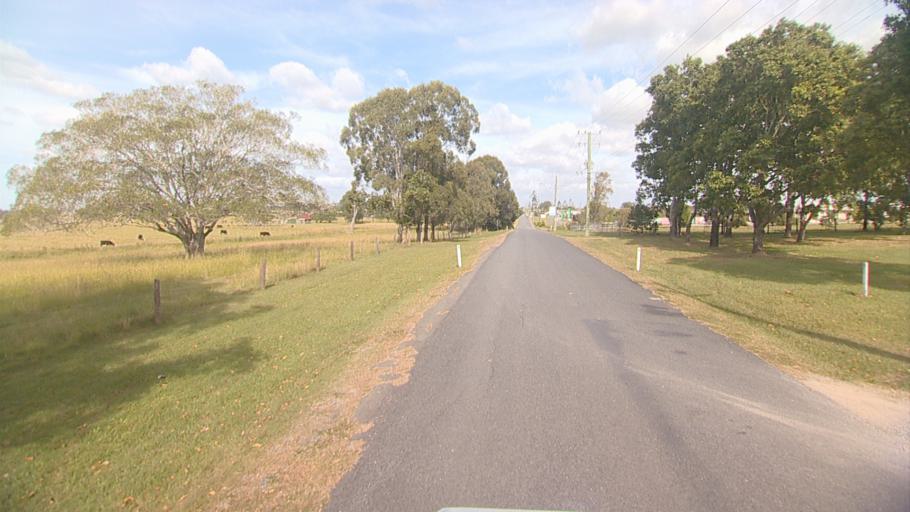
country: AU
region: Queensland
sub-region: Logan
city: Waterford West
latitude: -27.6827
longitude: 153.1584
